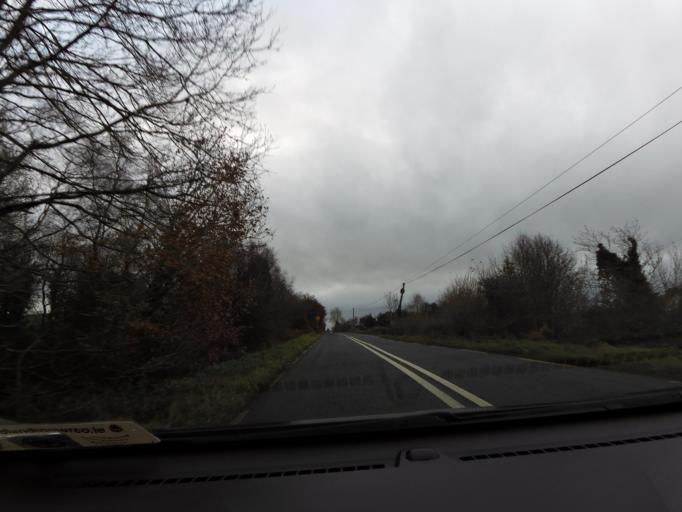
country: IE
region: Connaught
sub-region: County Galway
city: Portumna
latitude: 53.1433
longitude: -8.2561
